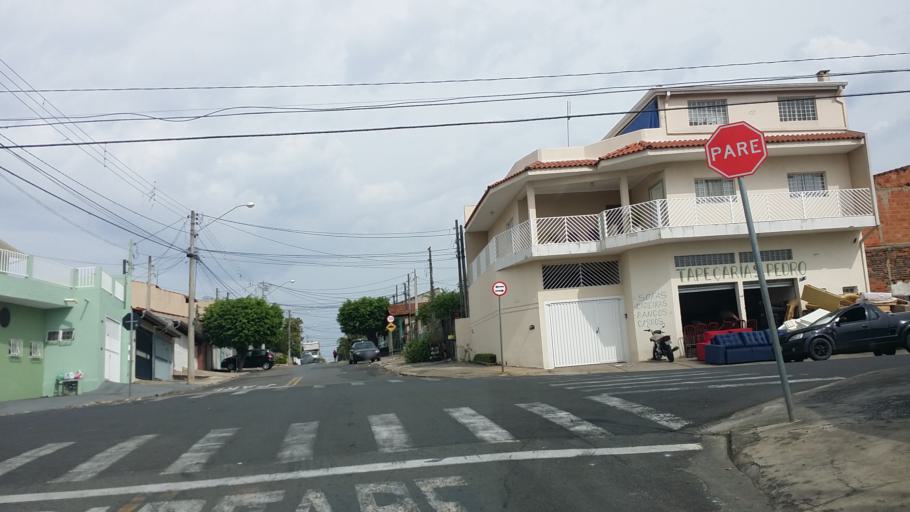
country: BR
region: Sao Paulo
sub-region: Indaiatuba
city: Indaiatuba
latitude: -23.1194
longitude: -47.2361
